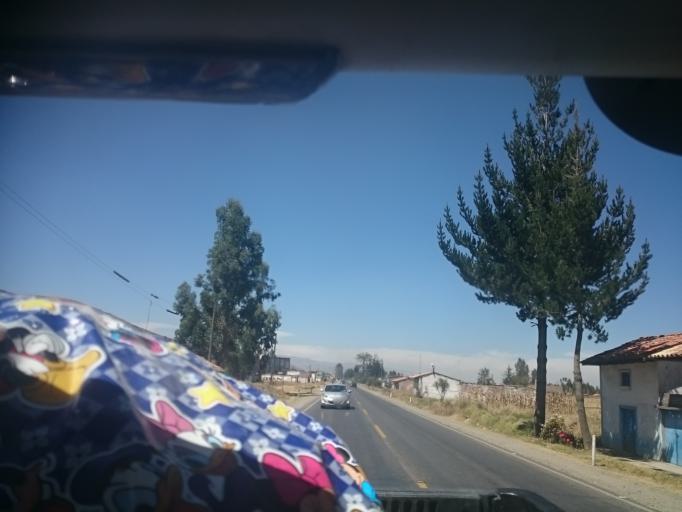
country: PE
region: Junin
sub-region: Provincia de Jauja
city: Huamali
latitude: -11.8075
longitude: -75.4323
